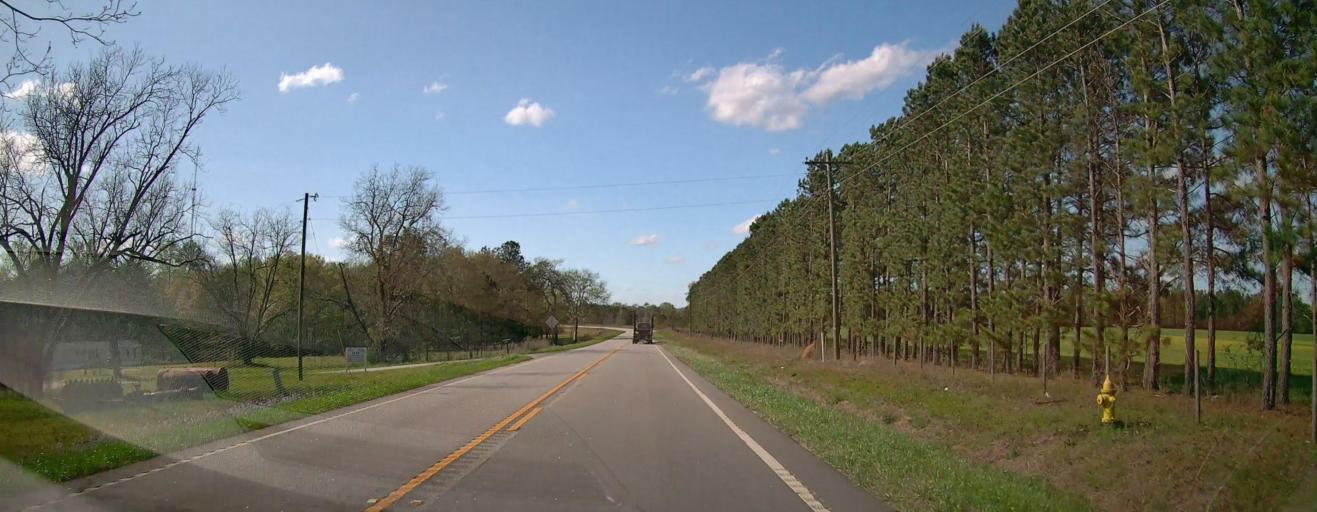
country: US
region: Georgia
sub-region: Baldwin County
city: Hardwick
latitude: 33.0750
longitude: -83.1383
